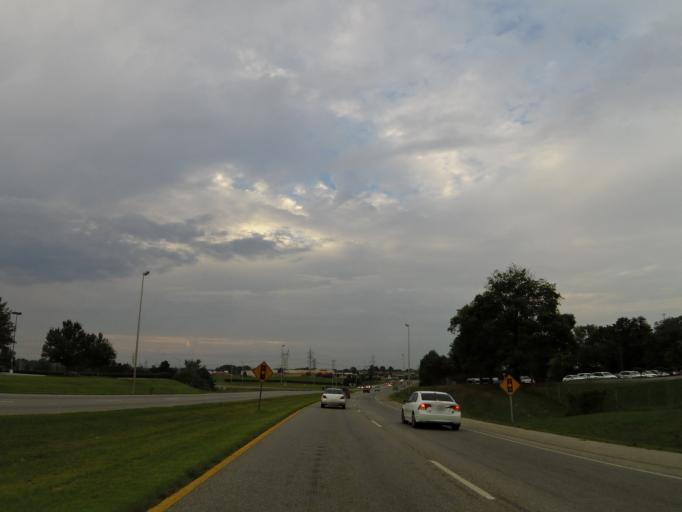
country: US
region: Tennessee
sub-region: Blount County
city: Maryville
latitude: 35.7474
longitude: -83.9948
